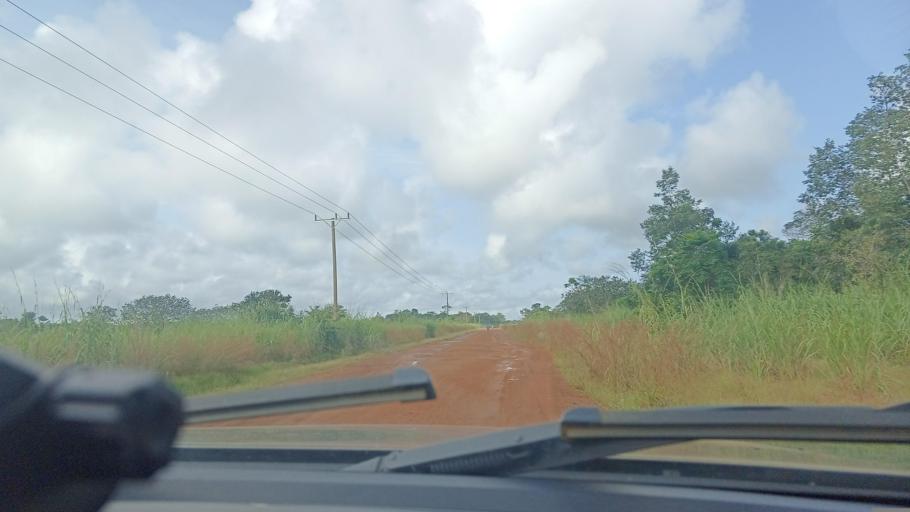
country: LR
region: Grand Cape Mount
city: Robertsport
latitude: 6.6914
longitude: -11.1112
